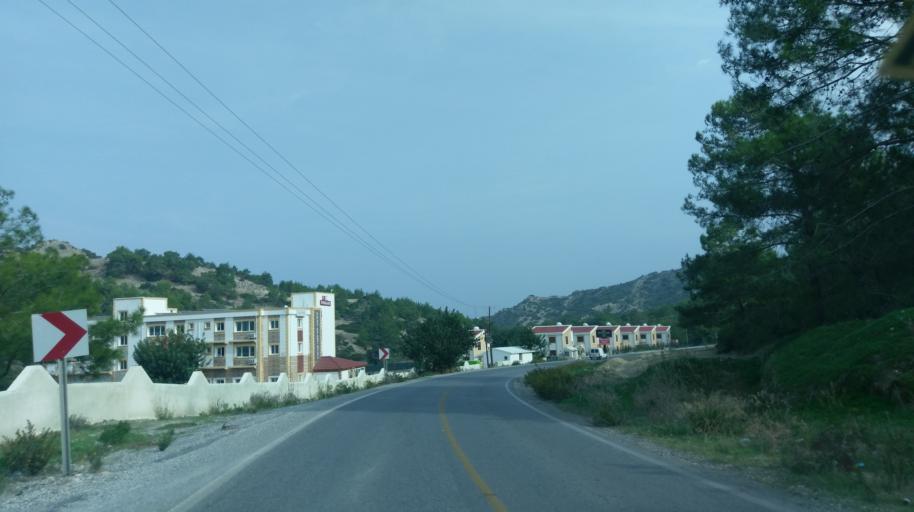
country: CY
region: Keryneia
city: Lapithos
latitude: 35.3425
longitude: 33.0752
